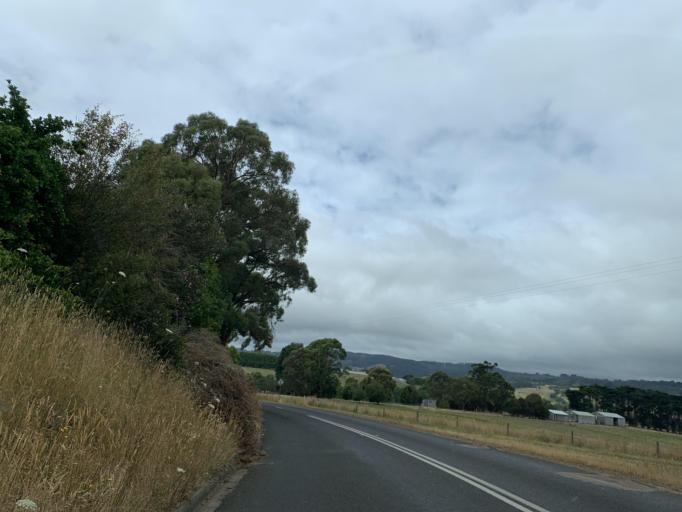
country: AU
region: Victoria
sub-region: Baw Baw
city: Warragul
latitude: -38.2390
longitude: 145.9289
